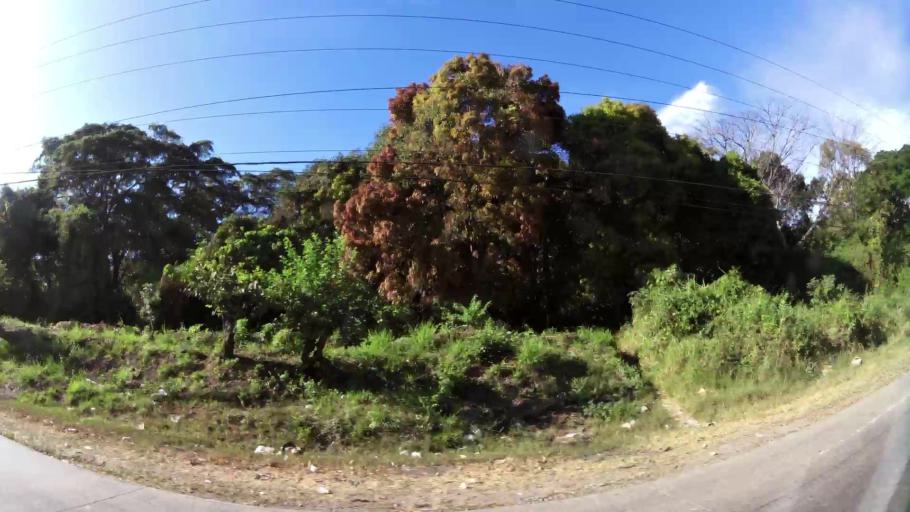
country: SV
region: Santa Ana
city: Santa Ana
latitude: 14.0247
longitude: -89.5326
